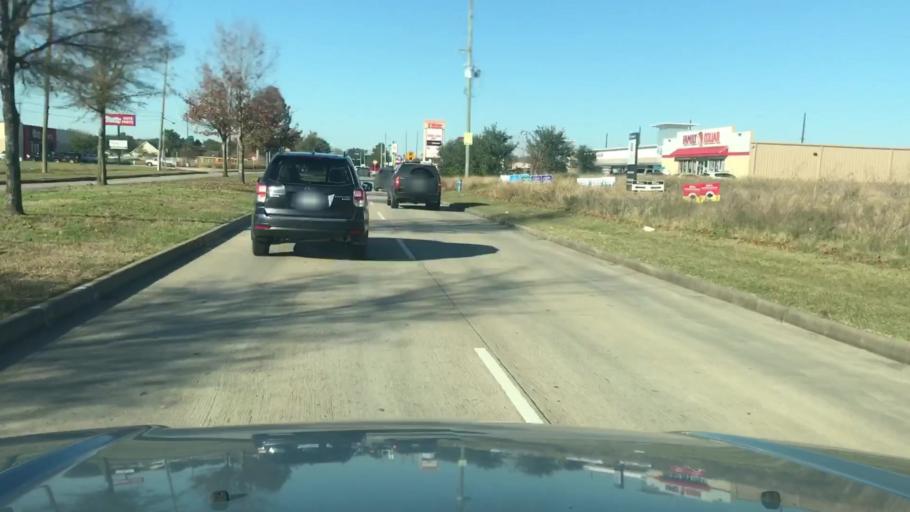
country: US
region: Texas
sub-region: Fort Bend County
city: Cinco Ranch
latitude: 29.8146
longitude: -95.7521
